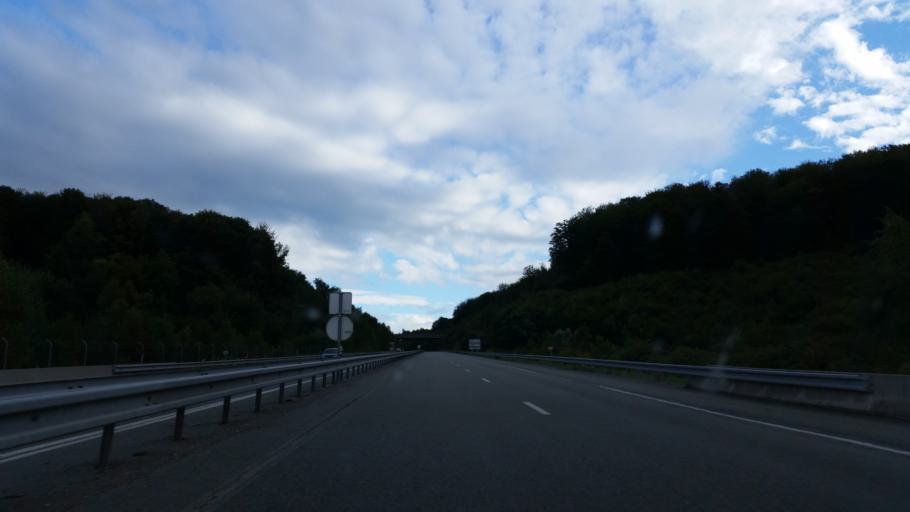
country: FR
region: Franche-Comte
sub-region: Departement de la Haute-Saone
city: Fougerolles
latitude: 47.8596
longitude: 6.3817
